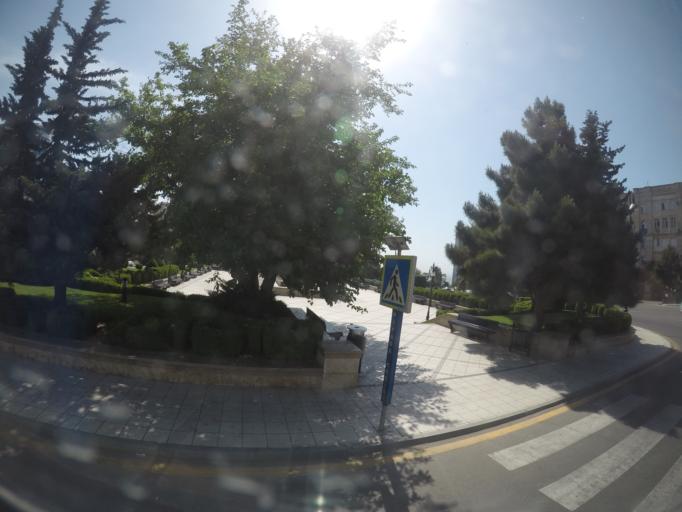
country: AZ
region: Baki
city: Badamdar
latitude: 40.3685
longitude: 49.8237
